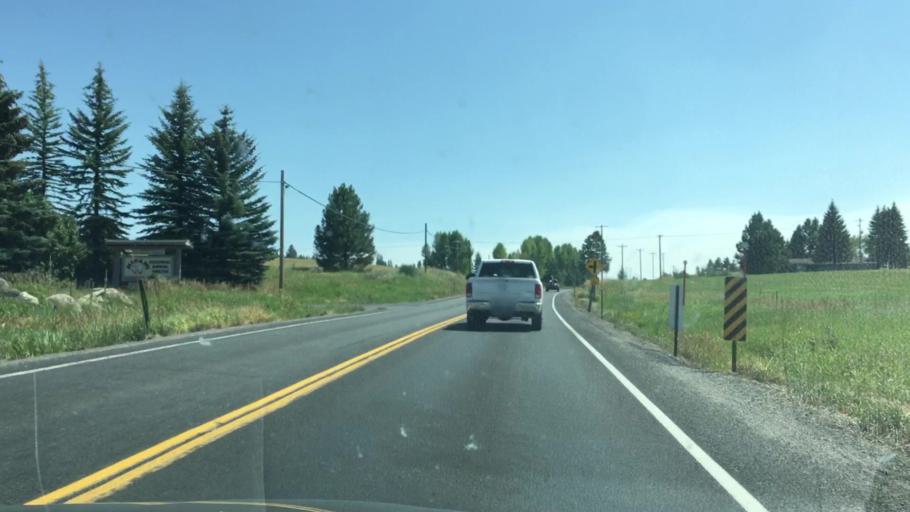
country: US
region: Idaho
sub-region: Valley County
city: McCall
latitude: 44.8852
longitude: -116.0912
